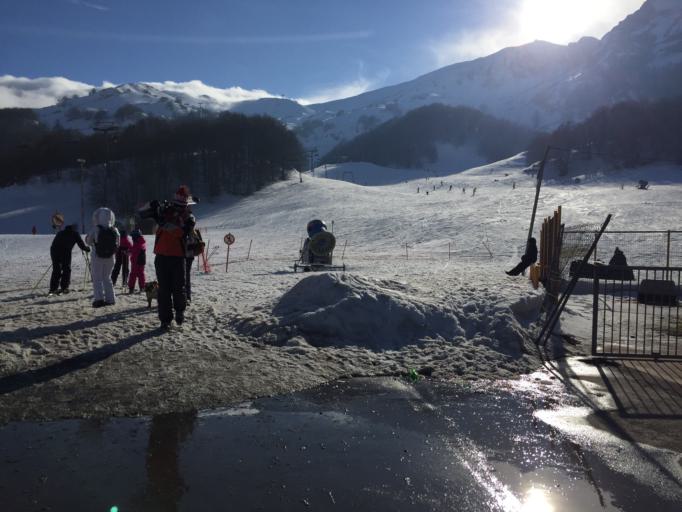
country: IT
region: Molise
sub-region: Provincia di Campobasso
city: San Massimo
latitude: 41.4614
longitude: 14.3891
